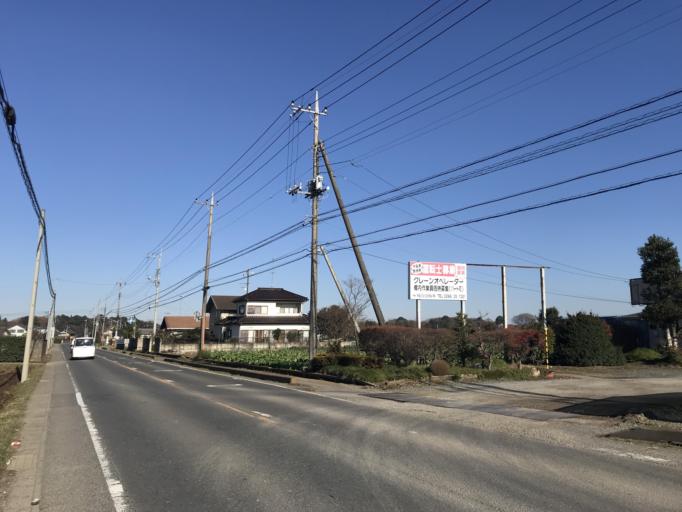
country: JP
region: Tochigi
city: Oyama
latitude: 36.2201
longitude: 139.8249
